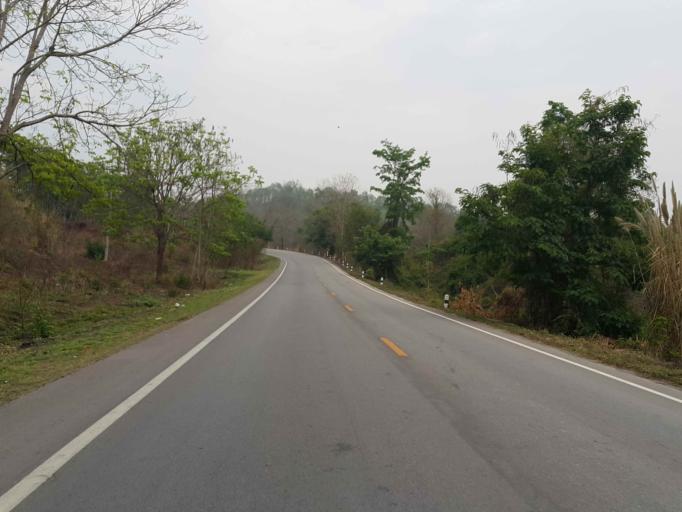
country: TH
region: Chiang Mai
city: Mae Taeng
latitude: 19.0698
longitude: 98.9693
